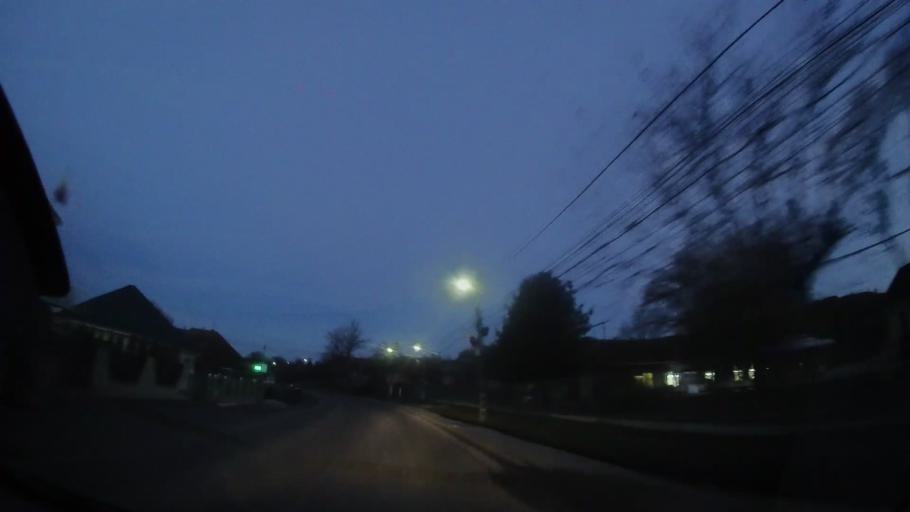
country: RO
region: Mures
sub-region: Comuna Sarmasu
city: Sarmasu
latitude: 46.7579
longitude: 24.1698
